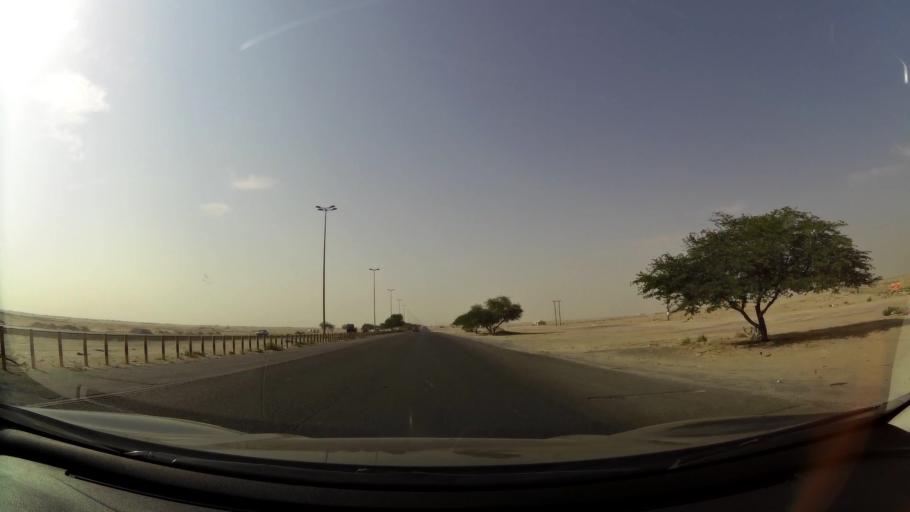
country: KW
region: Al Ahmadi
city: Al Ahmadi
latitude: 28.9250
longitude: 48.1039
